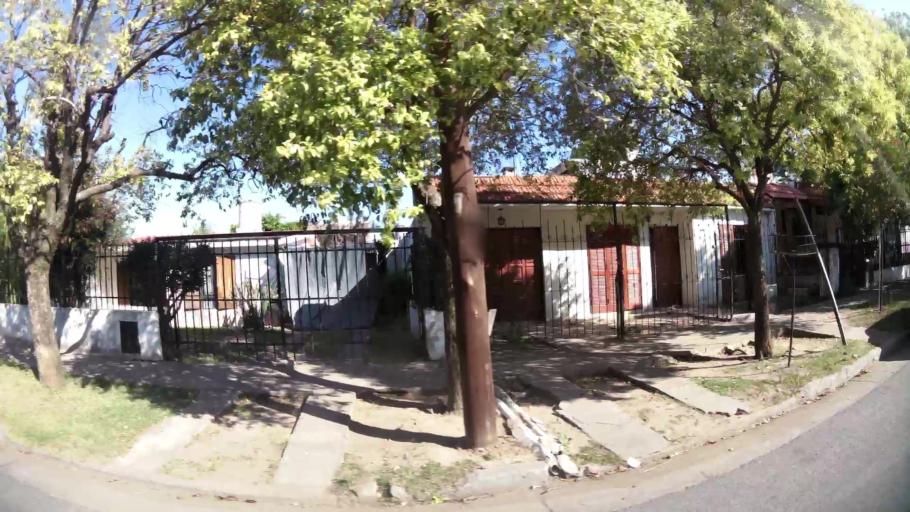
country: AR
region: Cordoba
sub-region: Departamento de Capital
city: Cordoba
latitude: -31.3621
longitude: -64.1953
